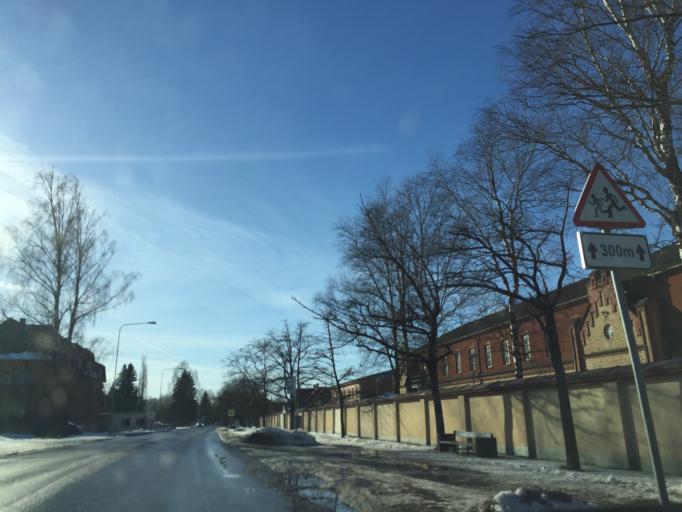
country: EE
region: Paernumaa
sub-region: Paernu linn
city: Parnu
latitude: 58.3776
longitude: 24.5309
